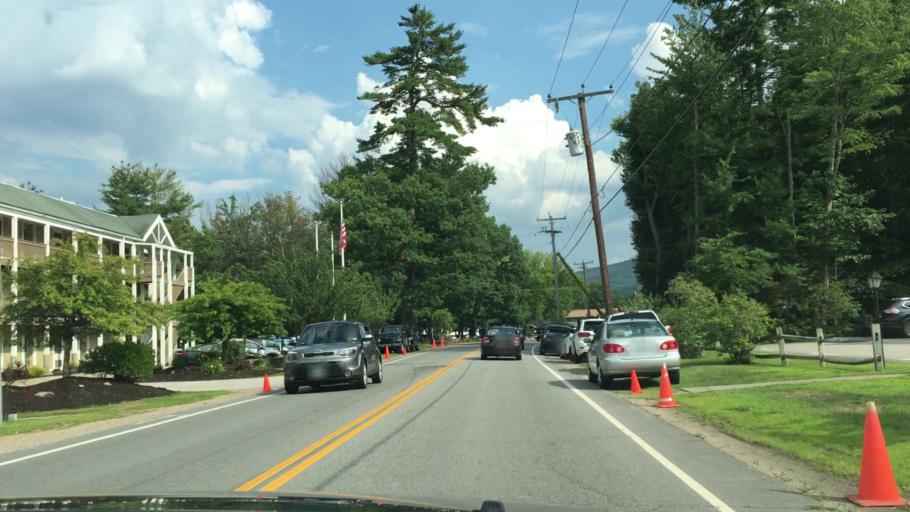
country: US
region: New Hampshire
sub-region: Belknap County
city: Gilford
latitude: 43.5816
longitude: -71.4102
